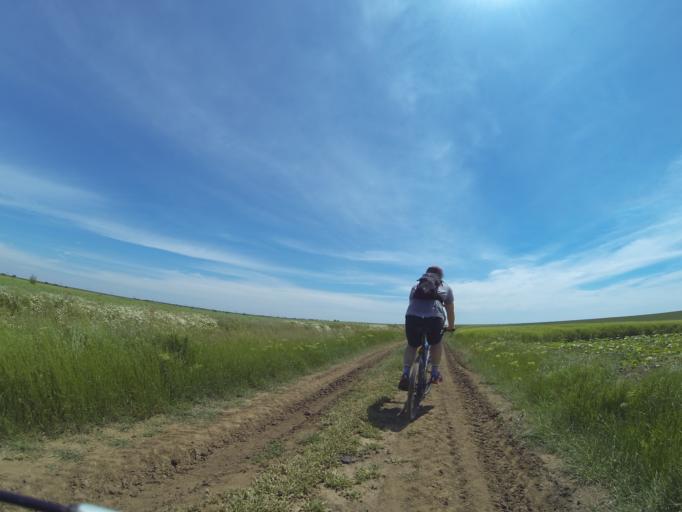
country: RO
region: Dolj
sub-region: Comuna Leu
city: Leu
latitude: 44.1892
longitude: 24.0494
